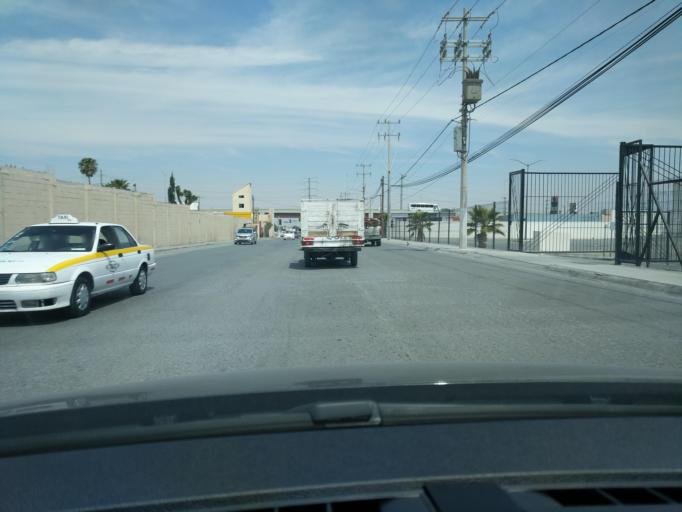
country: MX
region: Coahuila
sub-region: Arteaga
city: Arteaga
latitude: 25.4341
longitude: -100.9135
